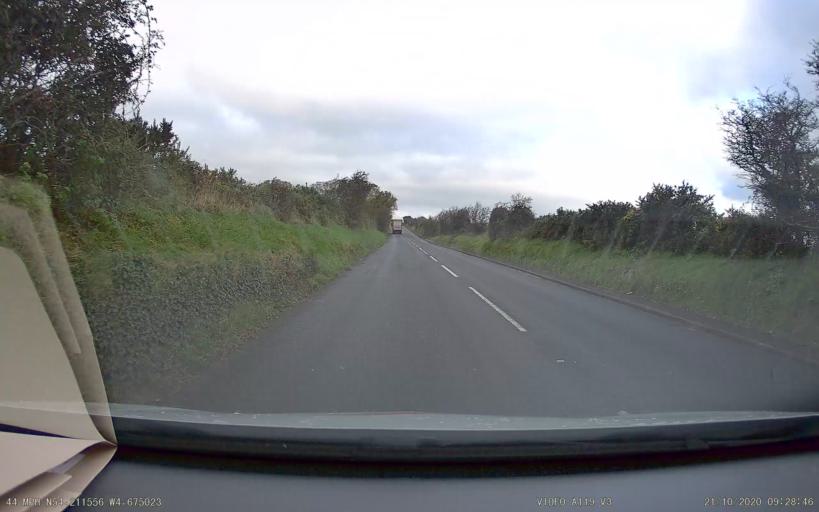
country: IM
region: Castletown
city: Castletown
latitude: 54.2116
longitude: -4.6750
